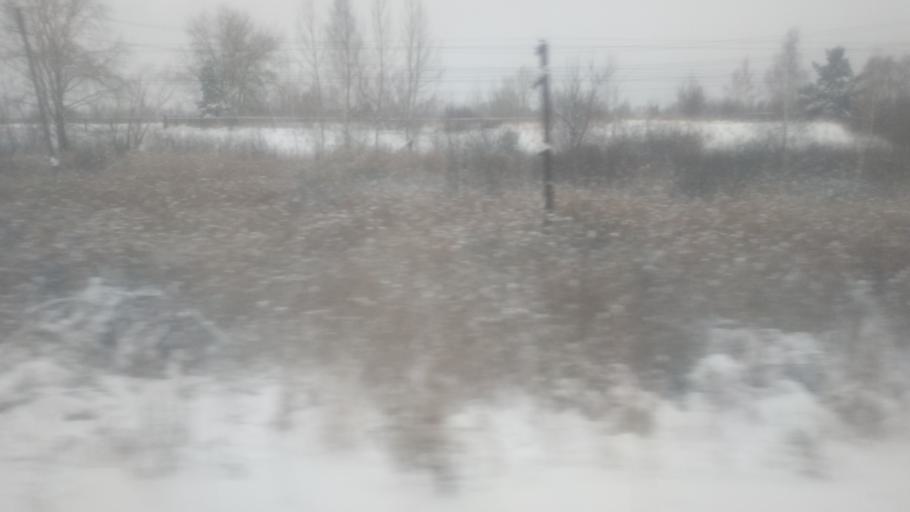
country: RU
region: Bashkortostan
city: Amzya
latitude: 56.2447
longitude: 54.6071
